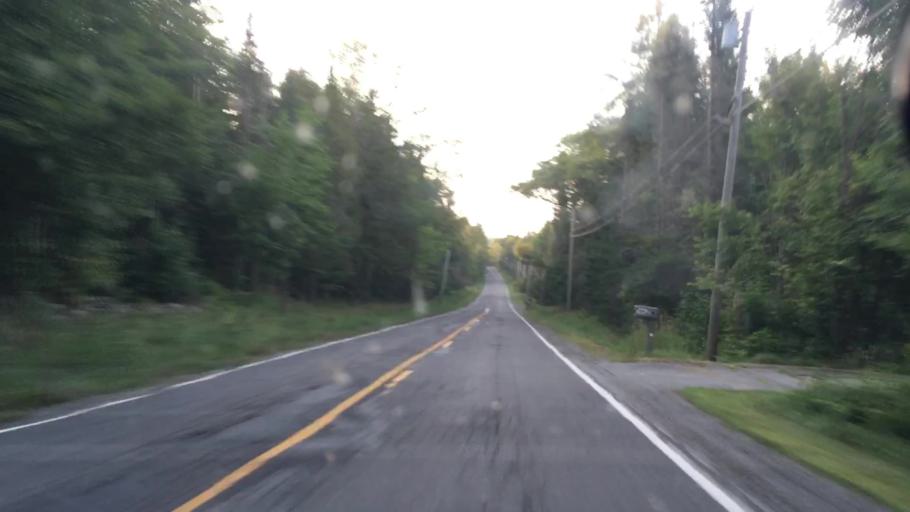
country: US
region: Maine
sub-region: Penobscot County
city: Hermon
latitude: 44.7026
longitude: -68.9468
